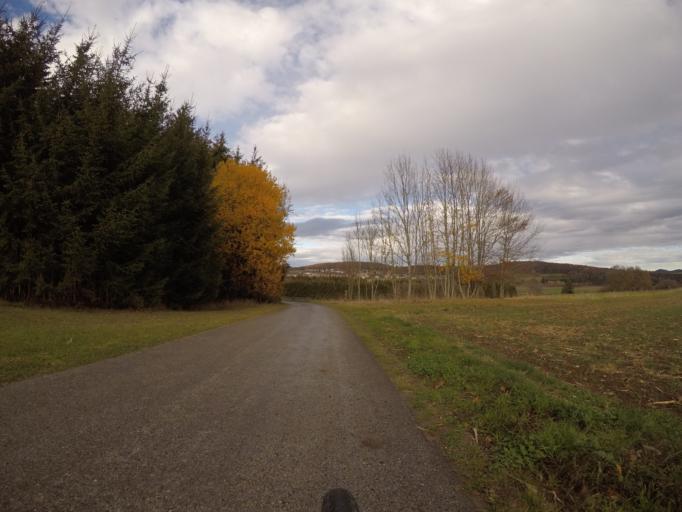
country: DE
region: Baden-Wuerttemberg
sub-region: Tuebingen Region
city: Sankt Johann
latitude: 48.4431
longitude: 9.3330
